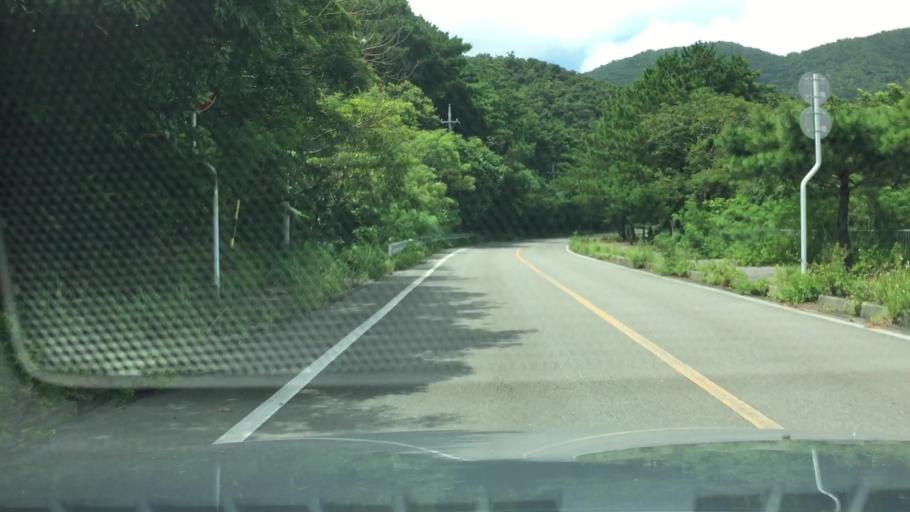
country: JP
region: Okinawa
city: Ishigaki
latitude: 24.4311
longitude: 124.2103
